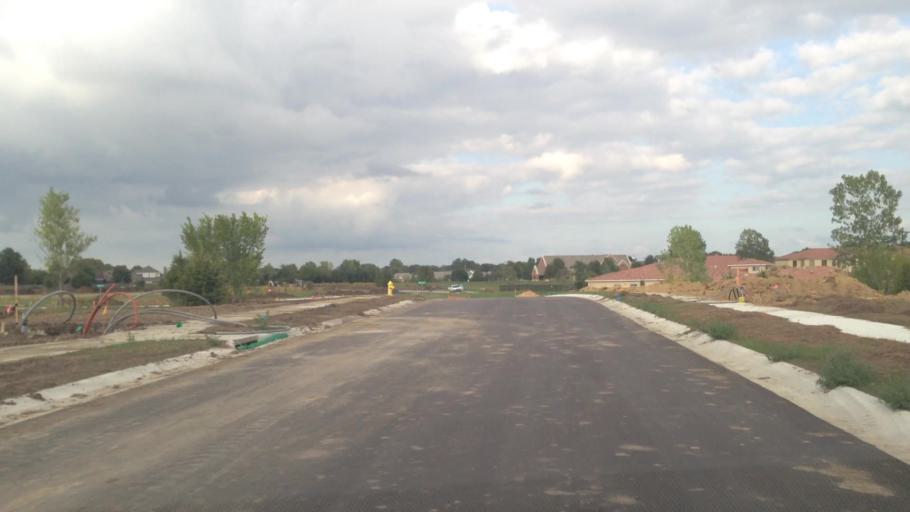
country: US
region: Kansas
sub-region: Douglas County
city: Lawrence
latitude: 38.9642
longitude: -95.3117
